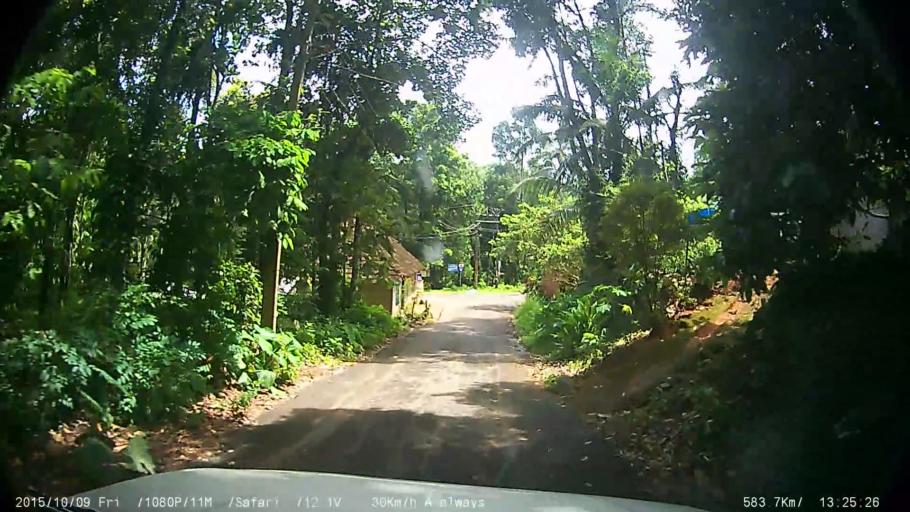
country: IN
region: Kerala
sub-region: Ernakulam
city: Muvattupuzha
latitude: 9.9222
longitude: 76.5675
